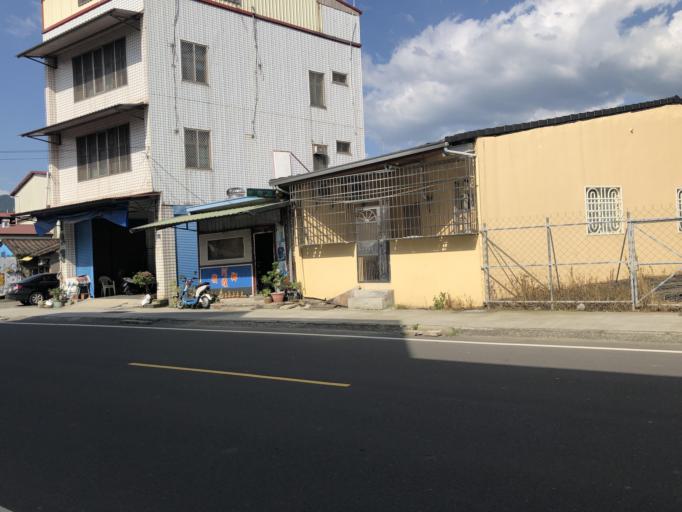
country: TW
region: Taiwan
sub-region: Pingtung
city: Pingtung
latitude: 22.8959
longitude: 120.5486
